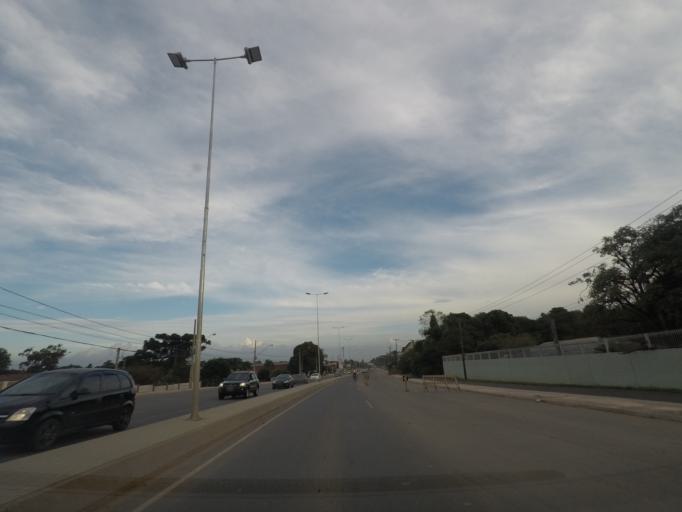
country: BR
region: Parana
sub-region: Colombo
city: Colombo
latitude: -25.3109
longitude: -49.2212
